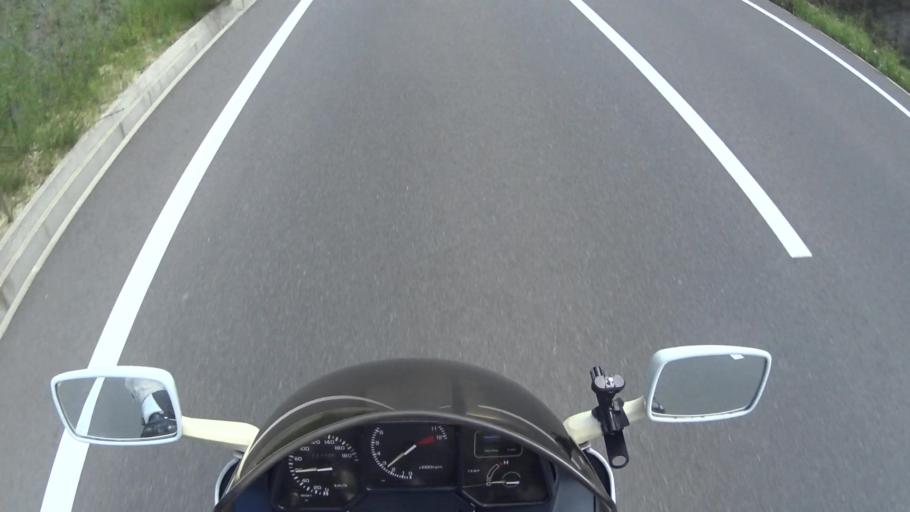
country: JP
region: Kyoto
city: Tanabe
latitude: 34.7826
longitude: 135.7557
